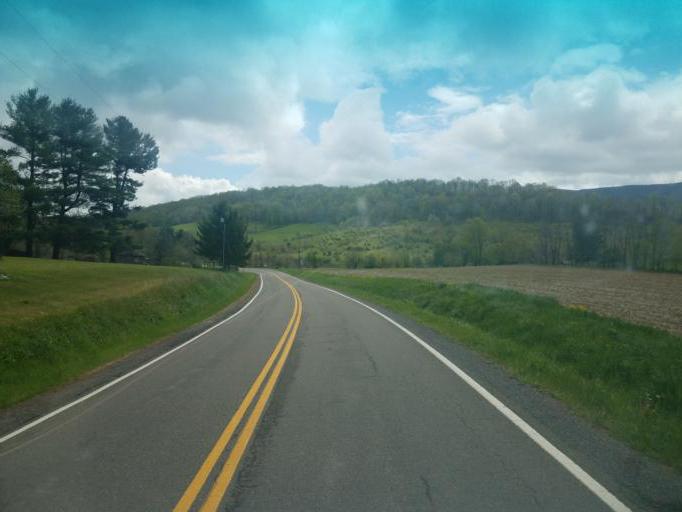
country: US
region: Virginia
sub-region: Wythe County
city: Rural Retreat
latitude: 37.0072
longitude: -81.3638
